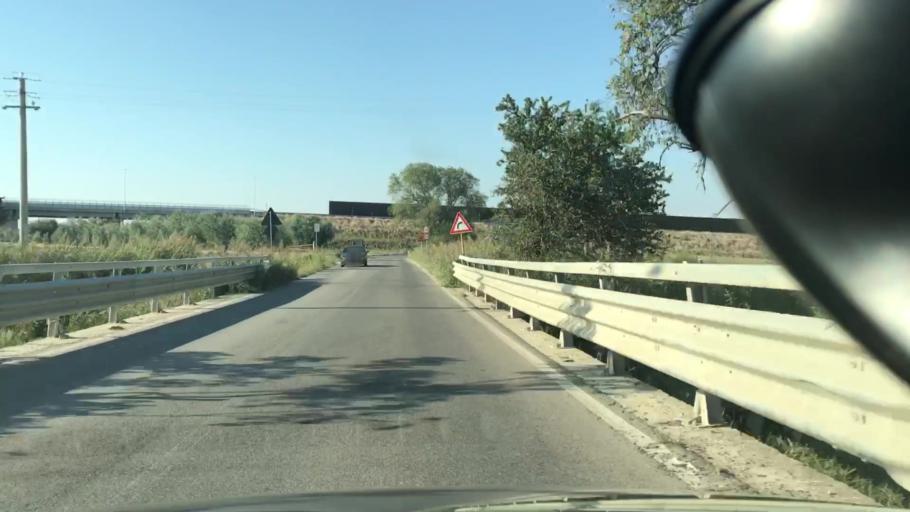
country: IT
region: Basilicate
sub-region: Provincia di Matera
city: La Martella
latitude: 40.6590
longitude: 16.5616
